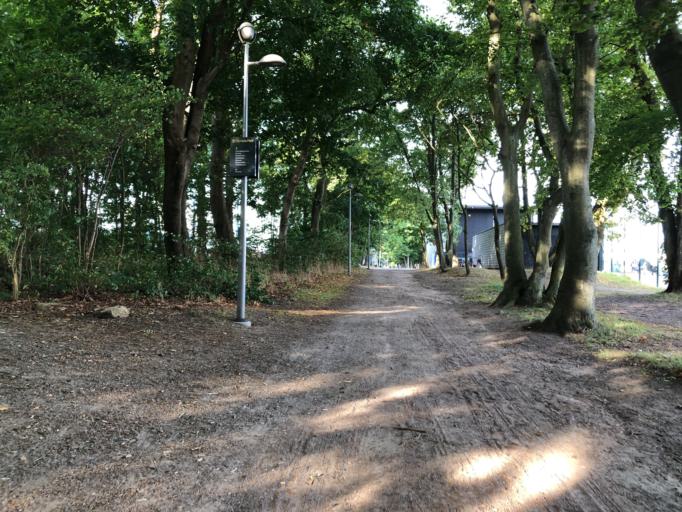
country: SE
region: Skane
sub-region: Helsingborg
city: Helsingborg
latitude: 56.0527
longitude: 12.7104
